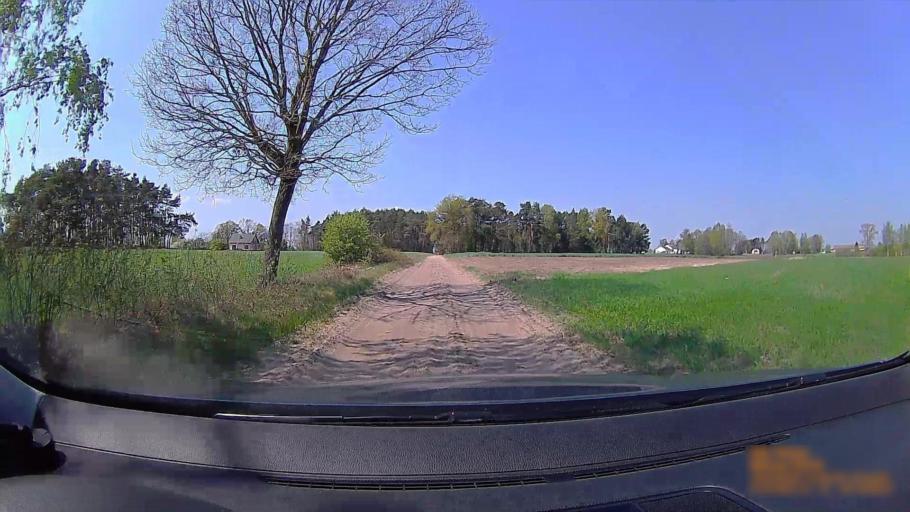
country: PL
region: Greater Poland Voivodeship
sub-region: Powiat koninski
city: Rychwal
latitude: 52.1023
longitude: 18.1768
